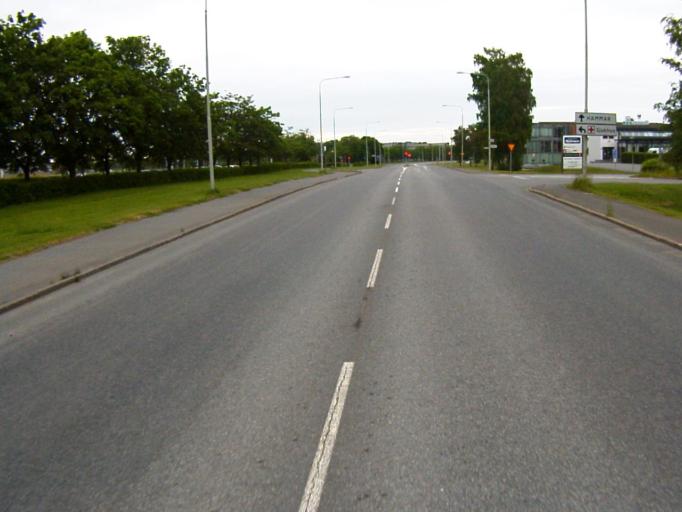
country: SE
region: Skane
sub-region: Kristianstads Kommun
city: Kristianstad
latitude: 56.0287
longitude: 14.1746
